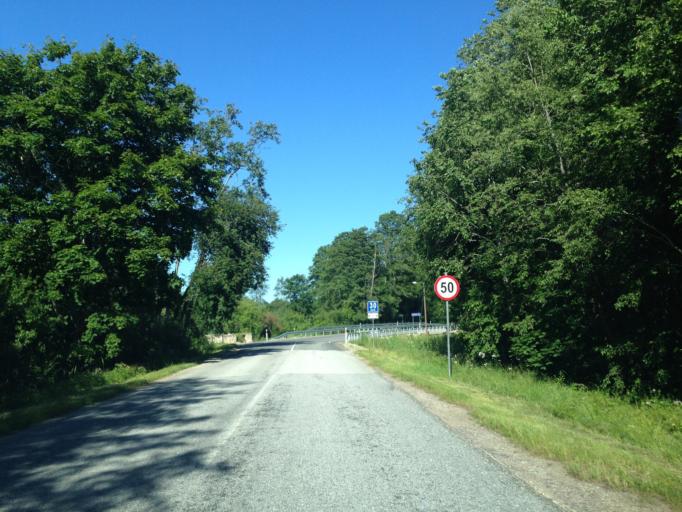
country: EE
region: Harju
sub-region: Raasiku vald
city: Raasiku
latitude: 59.4664
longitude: 25.2430
